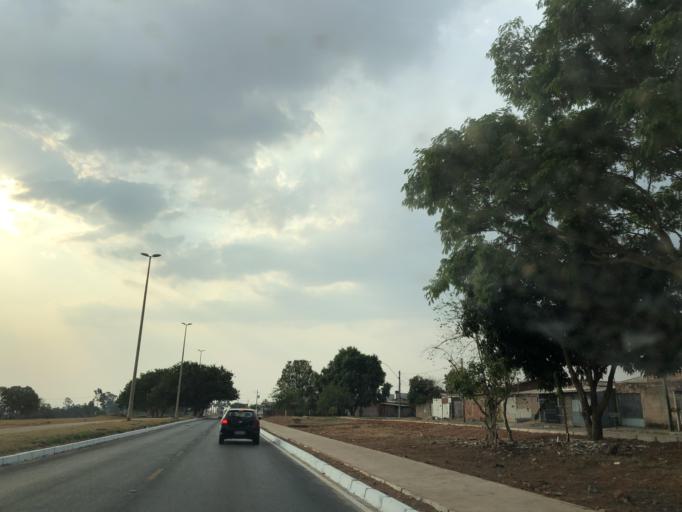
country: BR
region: Federal District
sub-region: Brasilia
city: Brasilia
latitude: -15.9259
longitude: -48.0543
